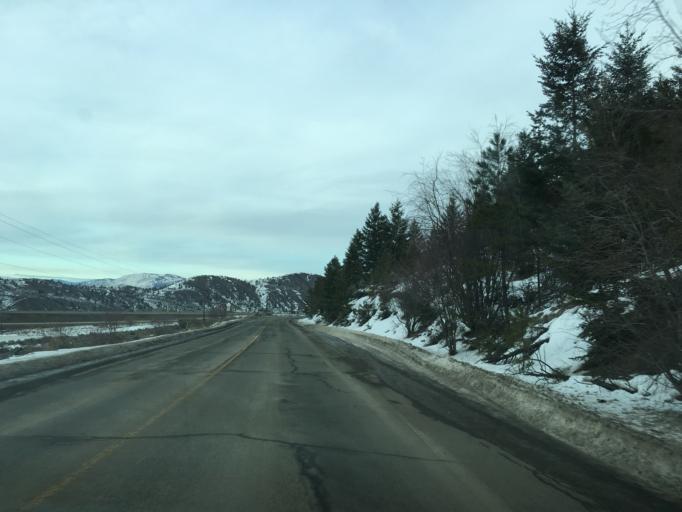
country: CA
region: British Columbia
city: Kamloops
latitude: 50.6626
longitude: -120.4339
